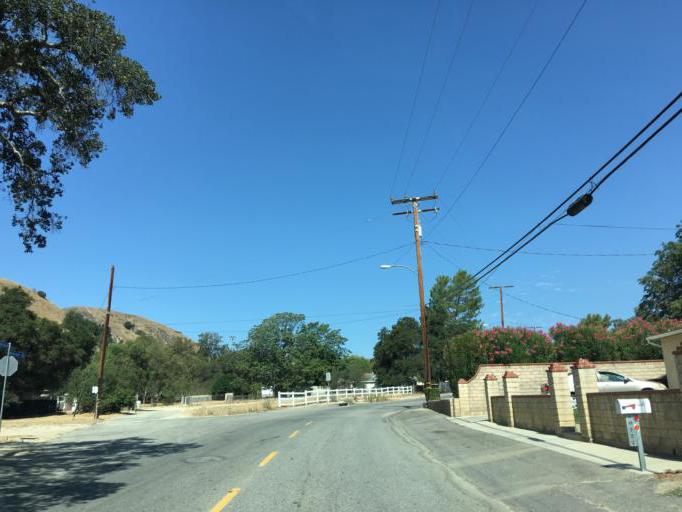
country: US
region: California
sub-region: Los Angeles County
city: Val Verde
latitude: 34.4459
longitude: -118.6608
